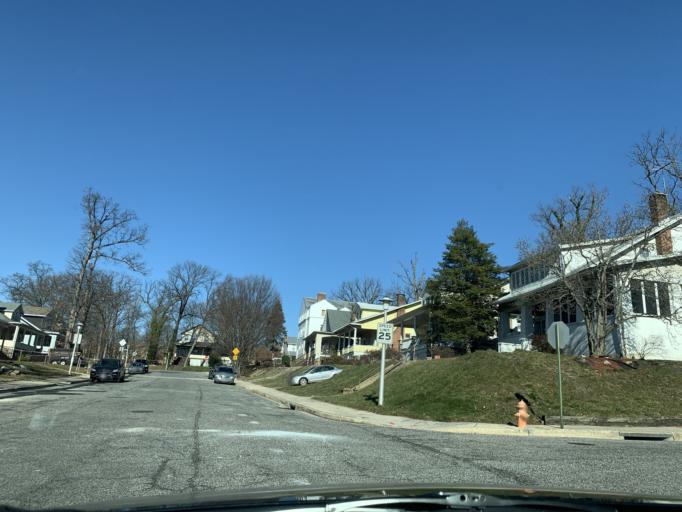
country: US
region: Maryland
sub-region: Baltimore County
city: Lochearn
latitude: 39.3192
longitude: -76.6794
